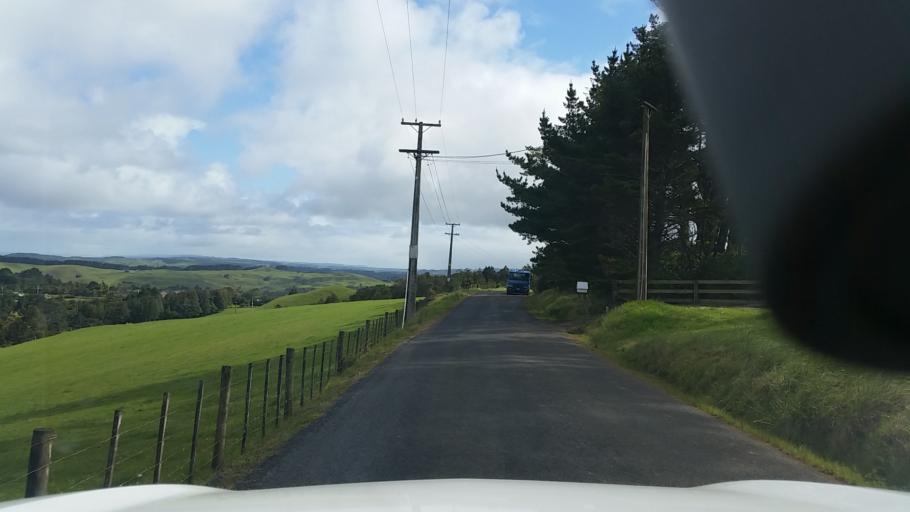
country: NZ
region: Auckland
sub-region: Auckland
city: Muriwai Beach
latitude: -36.8541
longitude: 174.4839
